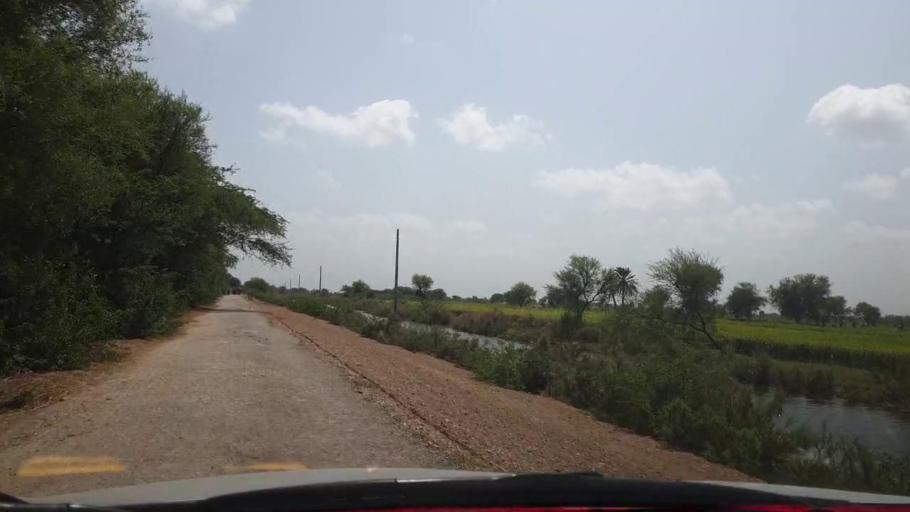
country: PK
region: Sindh
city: Talhar
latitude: 24.8951
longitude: 68.9059
